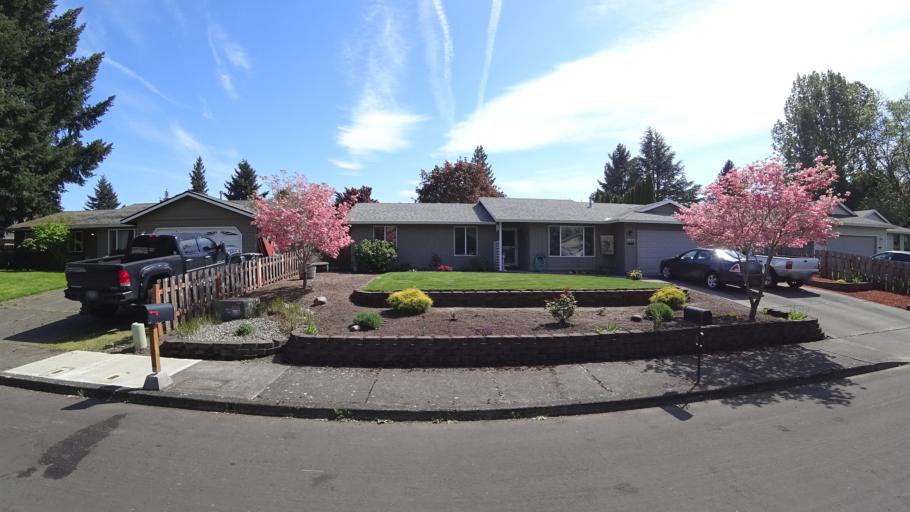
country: US
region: Oregon
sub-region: Washington County
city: Hillsboro
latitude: 45.5093
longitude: -122.9549
